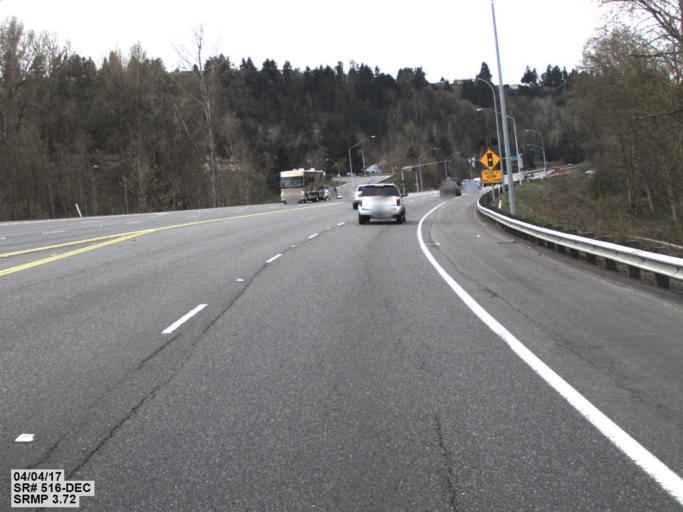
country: US
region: Washington
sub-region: King County
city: Kent
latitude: 47.3763
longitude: -122.2693
